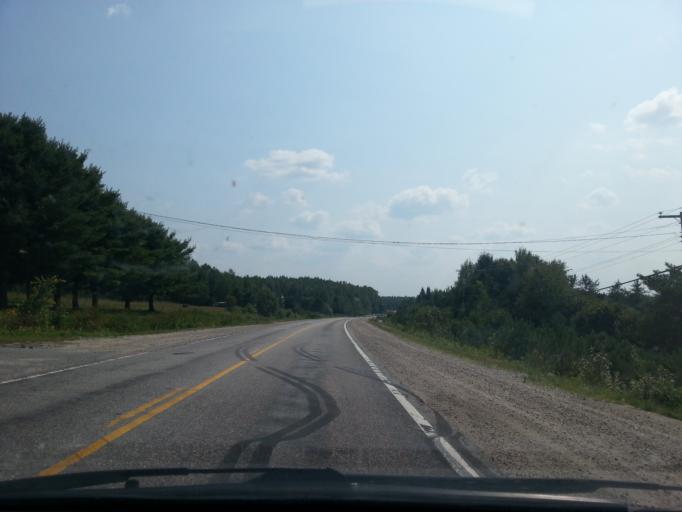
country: CA
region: Quebec
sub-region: Outaouais
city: Maniwaki
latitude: 46.0951
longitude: -76.0899
